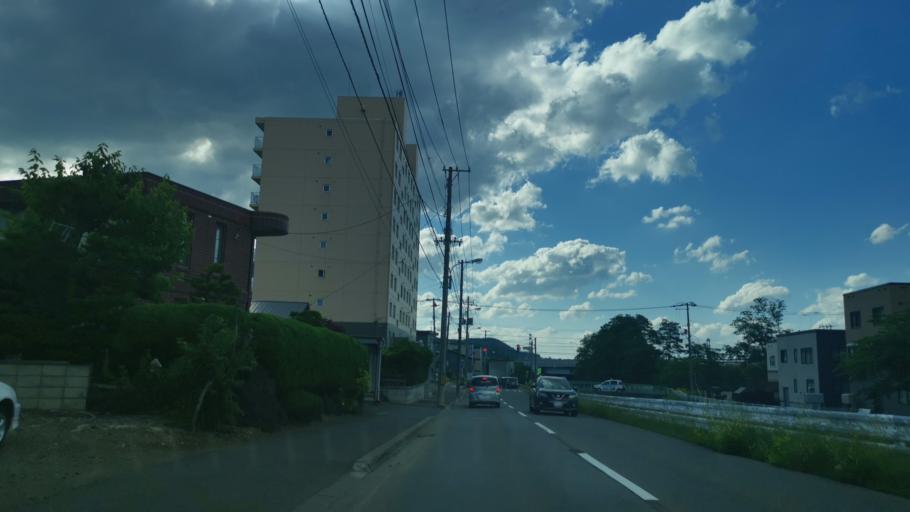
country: JP
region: Hokkaido
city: Sapporo
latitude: 43.0889
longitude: 141.2665
